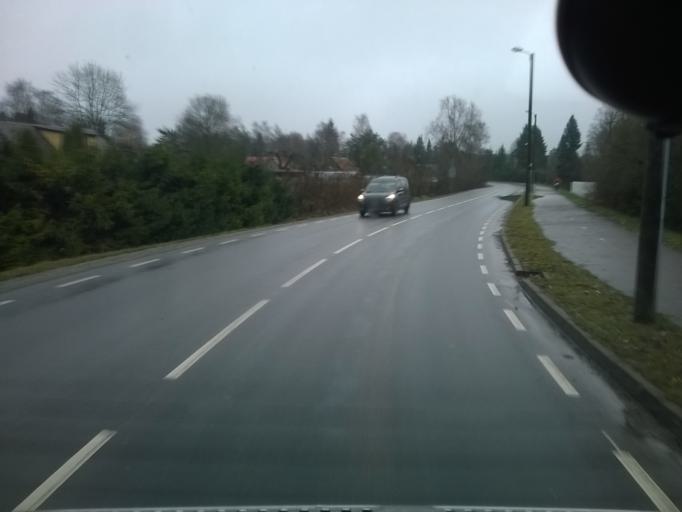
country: EE
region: Harju
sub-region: Saku vald
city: Saku
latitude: 59.2181
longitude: 24.6657
